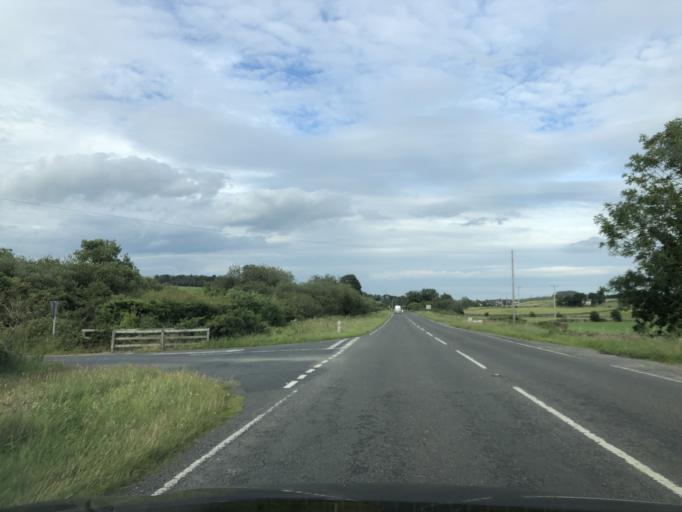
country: GB
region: Northern Ireland
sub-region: Down District
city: Castlewellan
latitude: 54.2478
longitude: -5.9726
